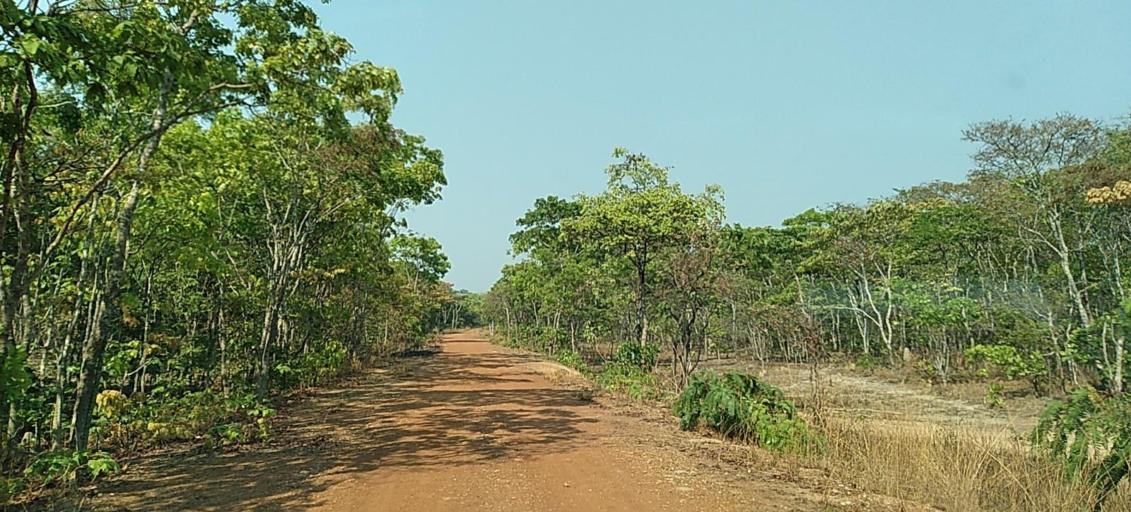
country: ZM
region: Copperbelt
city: Chingola
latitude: -12.8770
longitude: 27.4457
